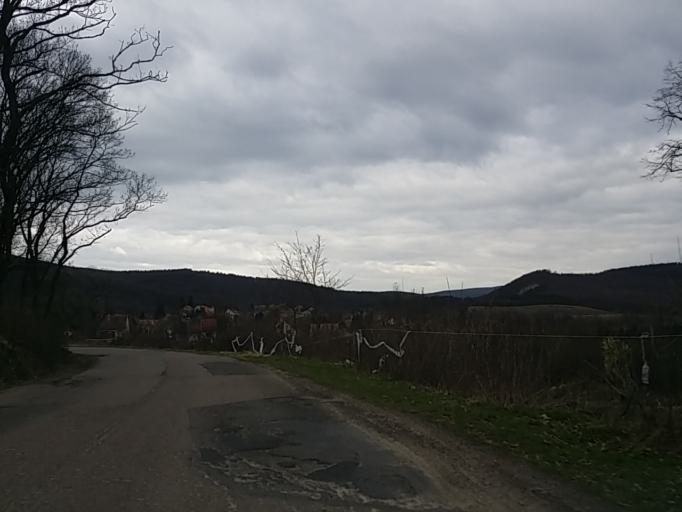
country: HU
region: Heves
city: Sirok
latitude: 47.8954
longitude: 20.1863
